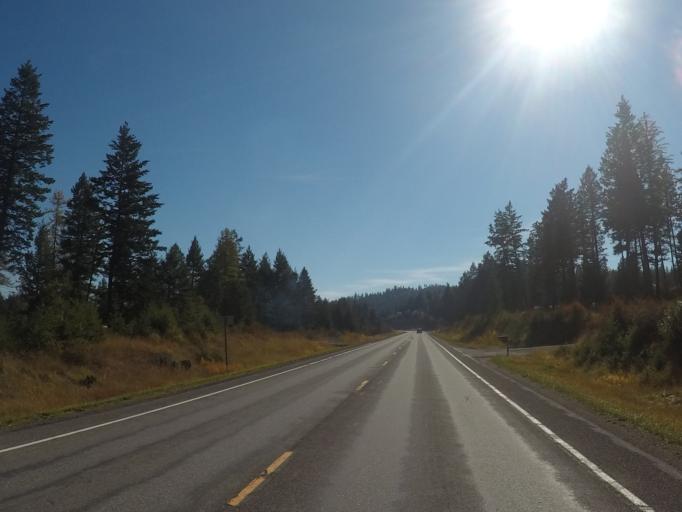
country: US
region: Montana
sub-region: Flathead County
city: Lakeside
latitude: 47.9964
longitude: -114.2112
